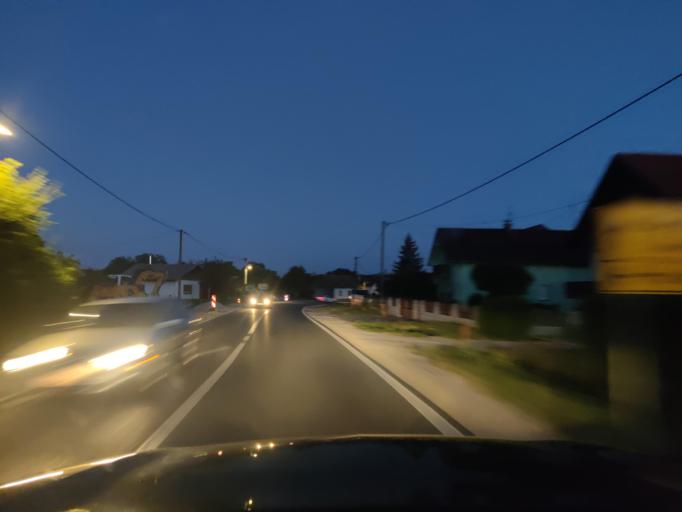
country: HR
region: Medimurska
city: Mackovec
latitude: 46.4474
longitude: 16.4318
